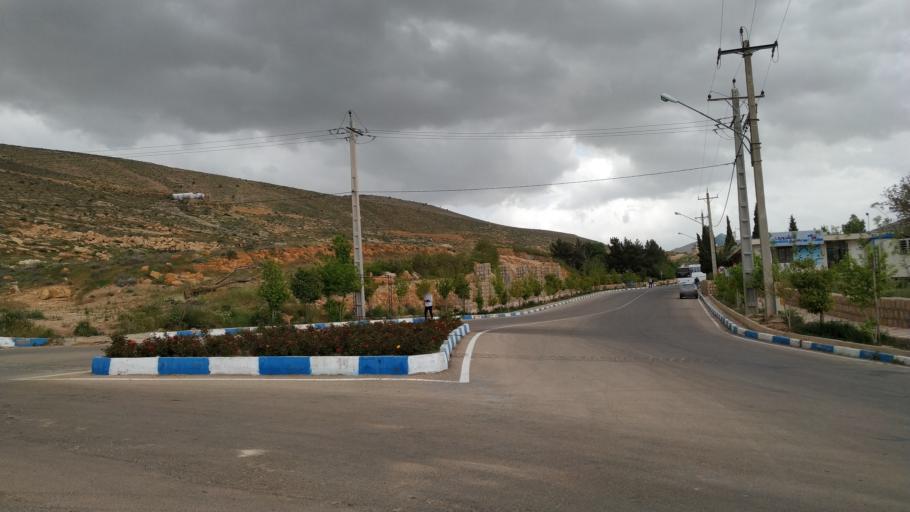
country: IR
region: Fars
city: Shiraz
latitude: 29.7673
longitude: 52.4805
